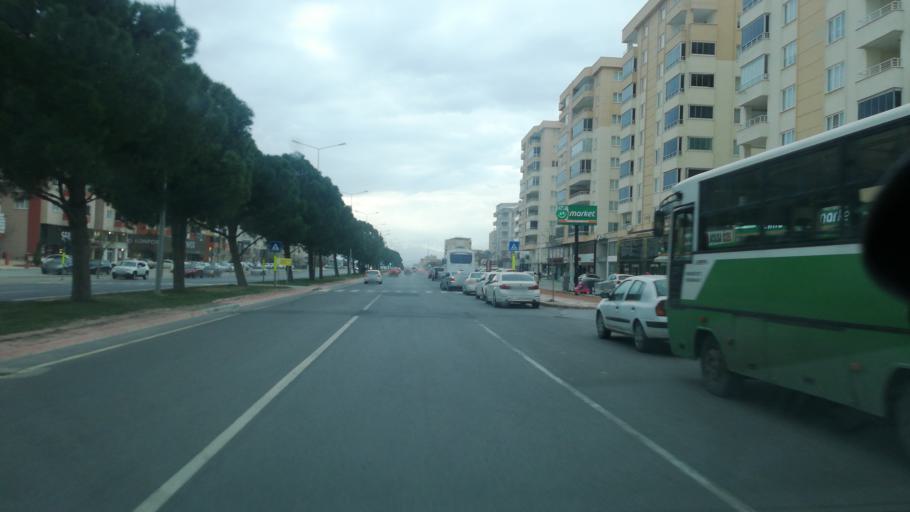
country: TR
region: Kahramanmaras
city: Kahramanmaras
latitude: 37.5948
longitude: 36.8541
